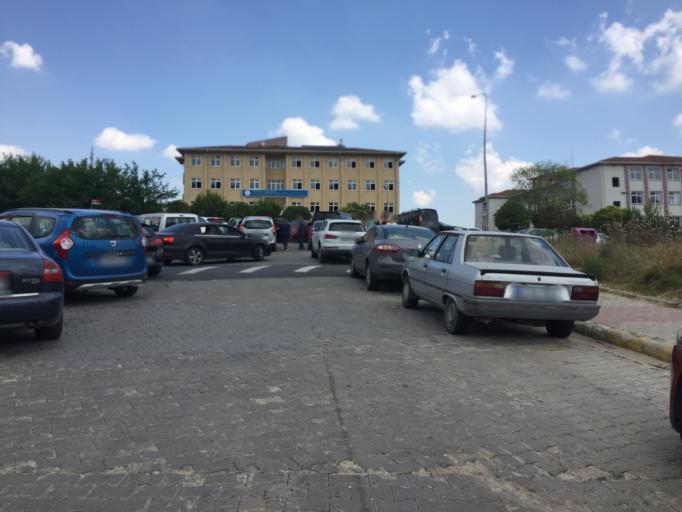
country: TR
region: Istanbul
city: Esenyurt
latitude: 41.0798
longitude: 28.6624
